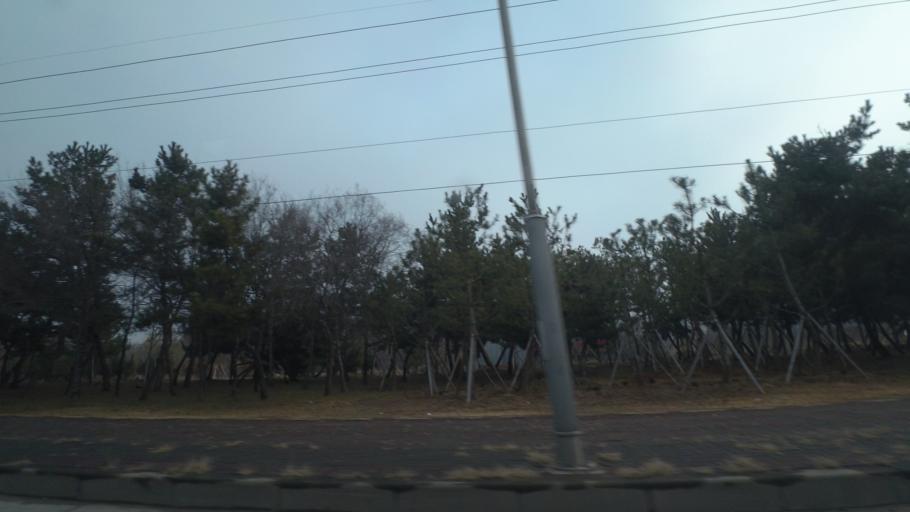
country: KR
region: Gyeonggi-do
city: Hwaseong-si
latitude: 36.9909
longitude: 126.8517
